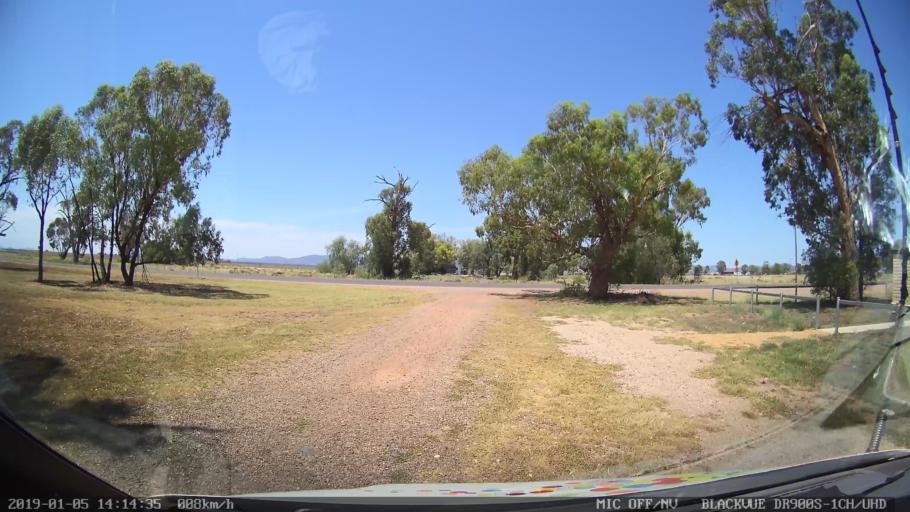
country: AU
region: New South Wales
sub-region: Liverpool Plains
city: Quirindi
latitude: -31.2469
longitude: 150.4682
